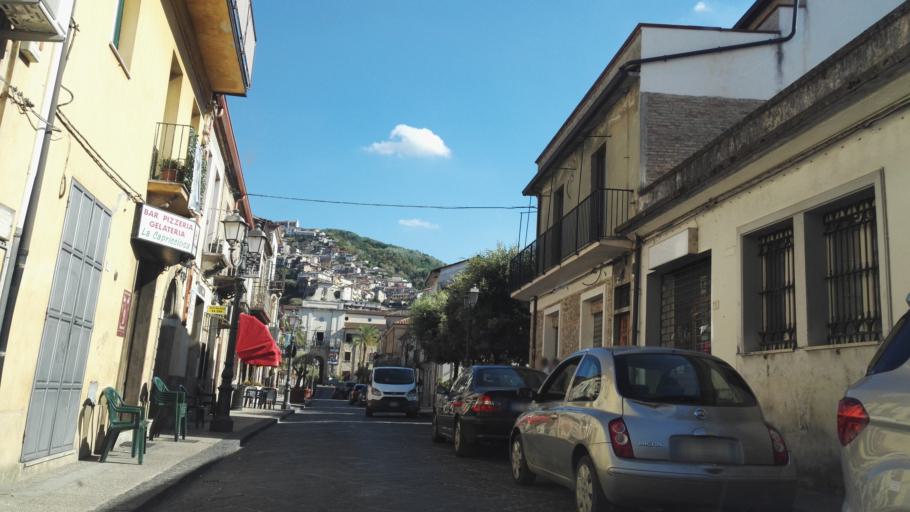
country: IT
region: Calabria
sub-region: Provincia di Vibo-Valentia
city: Sorianello
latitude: 38.5978
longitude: 16.2298
